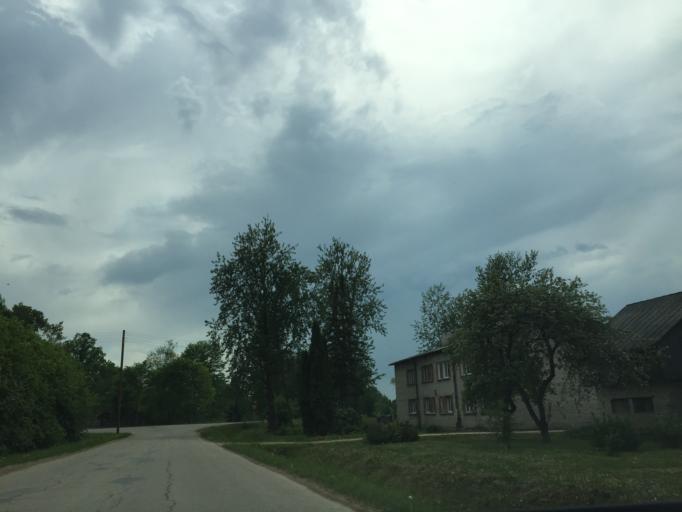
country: LV
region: Livani
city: Livani
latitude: 56.5358
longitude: 26.2407
